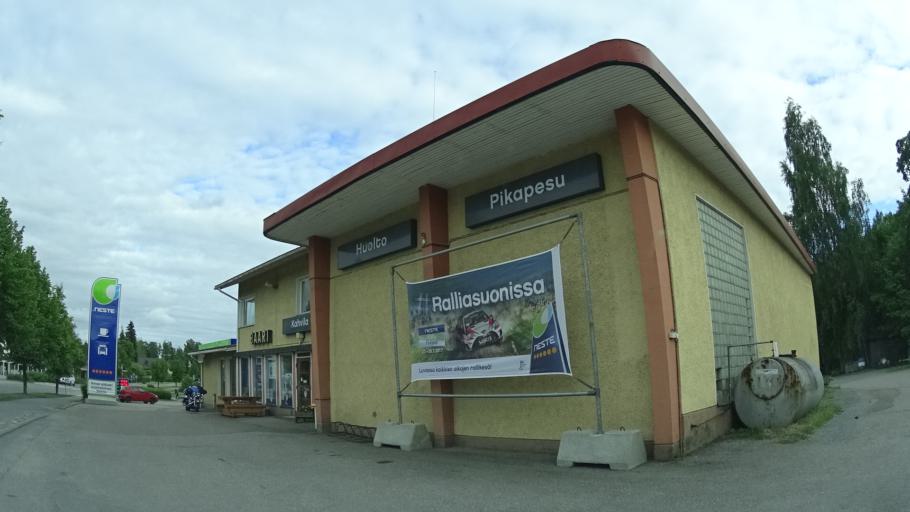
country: FI
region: Paijanne Tavastia
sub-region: Lahti
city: Sysmae
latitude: 61.5016
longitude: 25.6894
